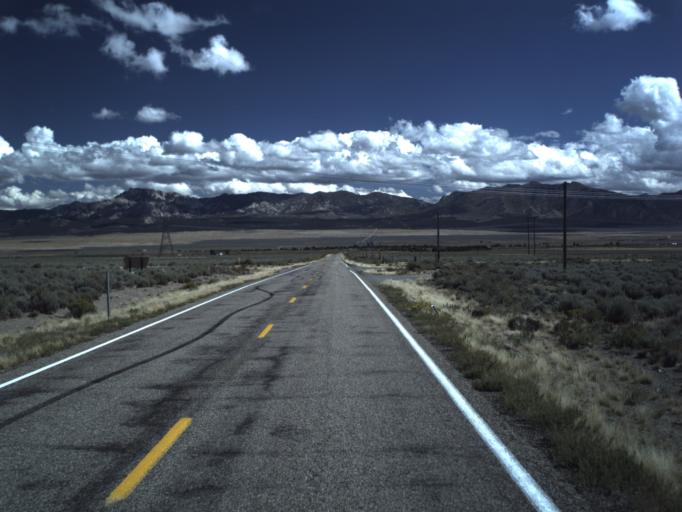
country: US
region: Utah
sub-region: Beaver County
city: Milford
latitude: 38.4114
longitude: -113.0673
